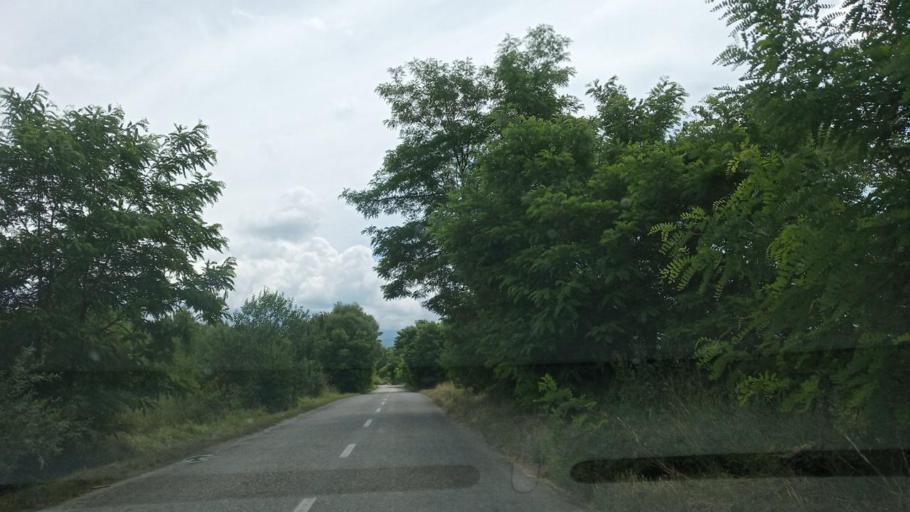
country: RO
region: Sibiu
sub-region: Comuna Porumbacu de Jos
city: Porumbacu de Jos
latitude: 45.7368
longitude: 24.4667
